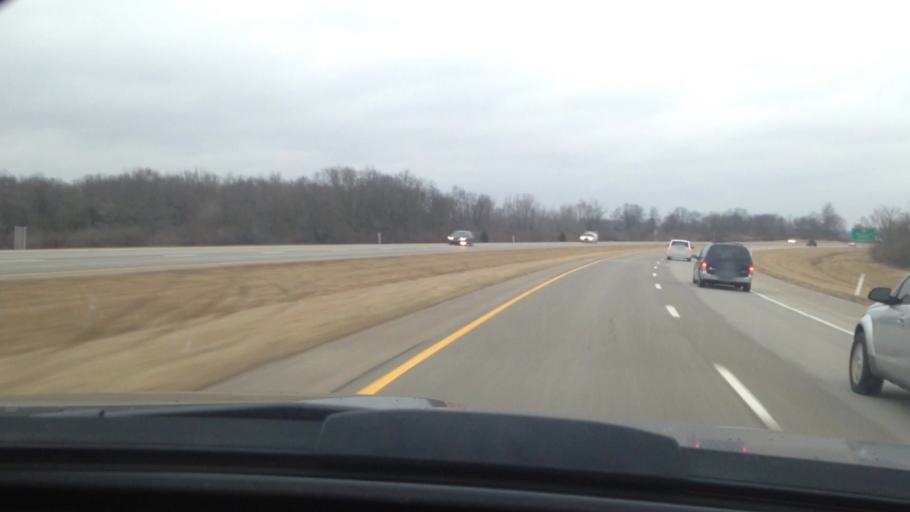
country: US
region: Indiana
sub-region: Delaware County
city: Muncie
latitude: 40.1578
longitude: -85.3534
